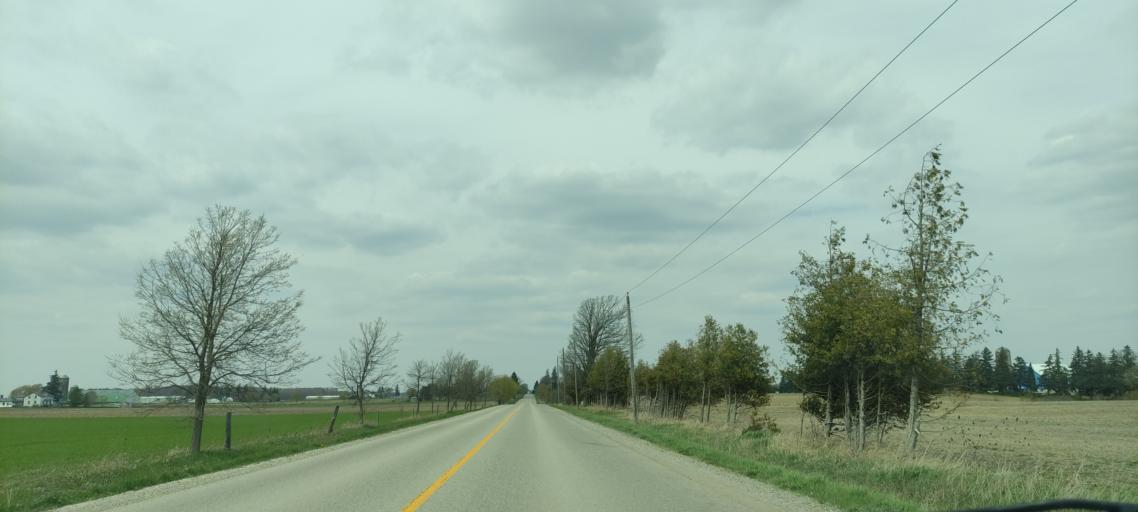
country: CA
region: Ontario
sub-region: Oxford County
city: Woodstock
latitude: 43.3023
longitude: -80.7755
